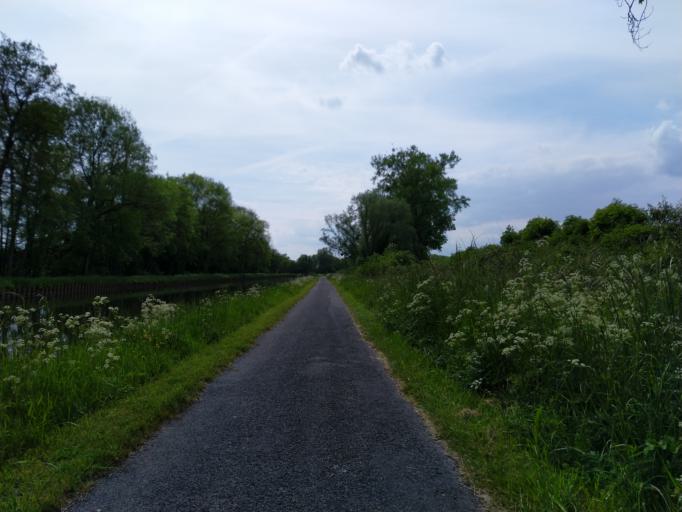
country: FR
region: Picardie
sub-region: Departement de l'Aisne
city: Boue
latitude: 49.9968
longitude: 3.6794
